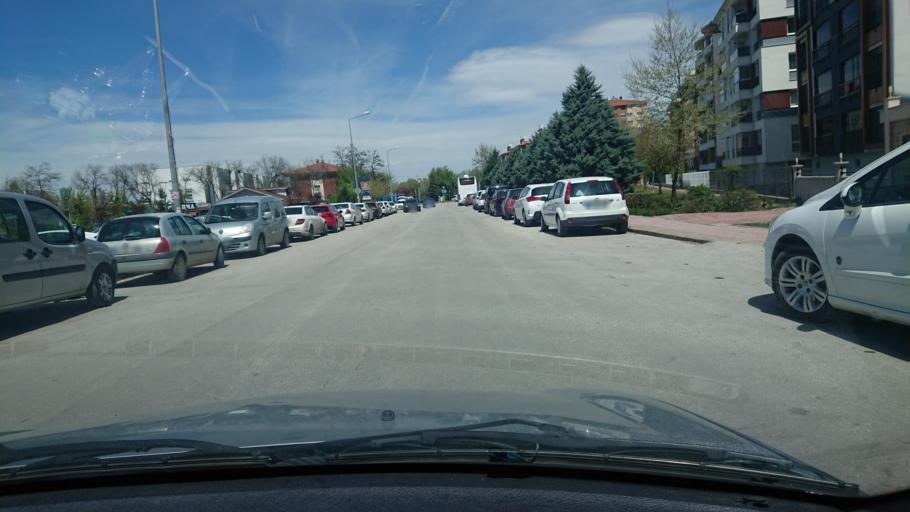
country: TR
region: Eskisehir
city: Eskisehir
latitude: 39.7656
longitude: 30.4973
